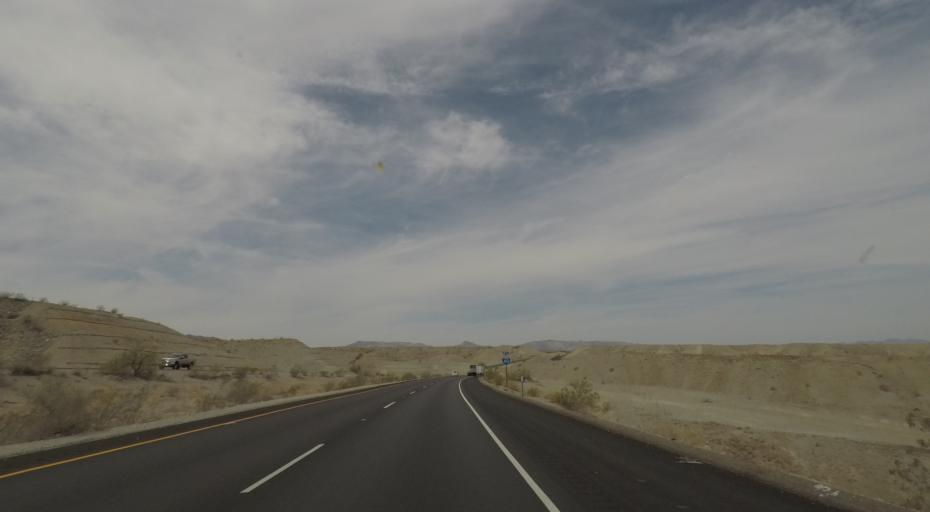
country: US
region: California
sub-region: San Bernardino County
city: Needles
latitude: 34.7177
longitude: -114.5269
